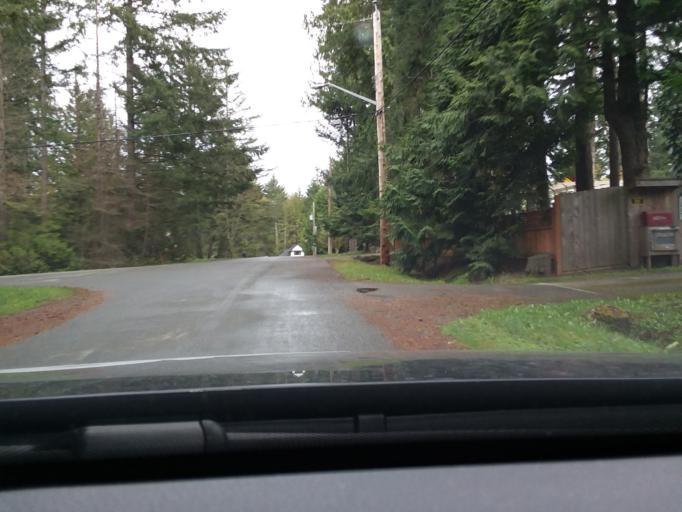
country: CA
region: British Columbia
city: North Saanich
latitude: 48.6163
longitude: -123.4210
